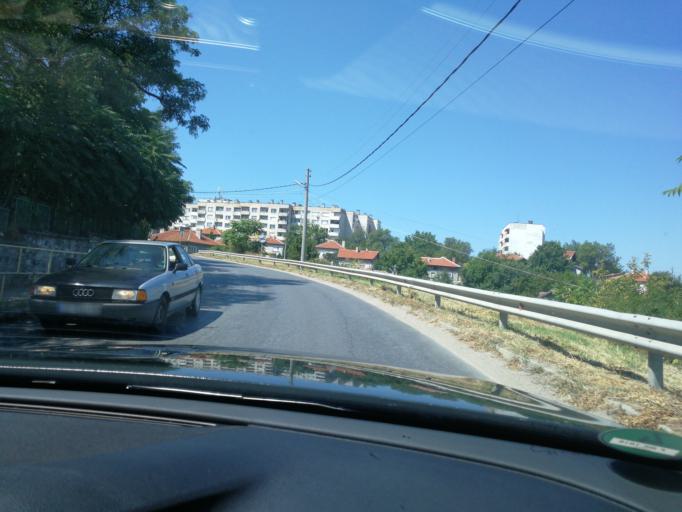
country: BG
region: Khaskovo
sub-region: Obshtina Topolovgrad
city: Topolovgrad
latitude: 42.0847
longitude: 26.3306
